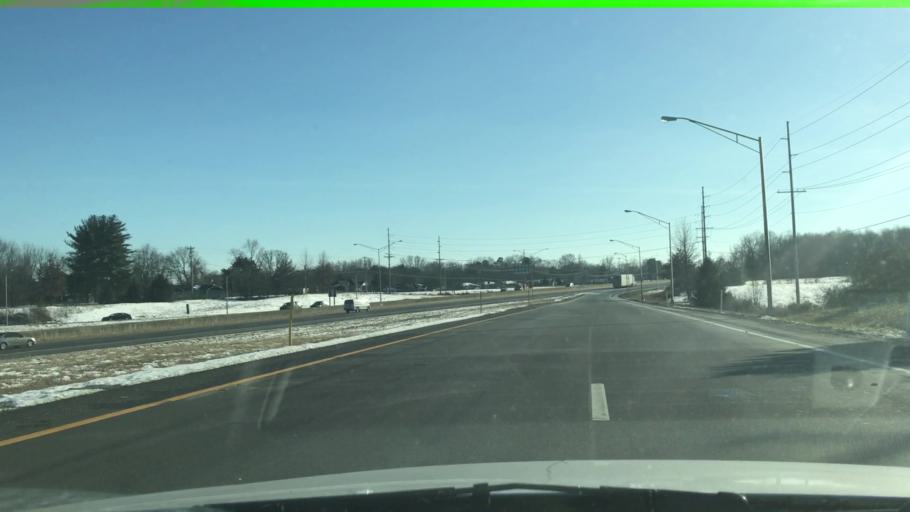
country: US
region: Kentucky
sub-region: Warren County
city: Bowling Green
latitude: 36.9767
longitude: -86.3924
